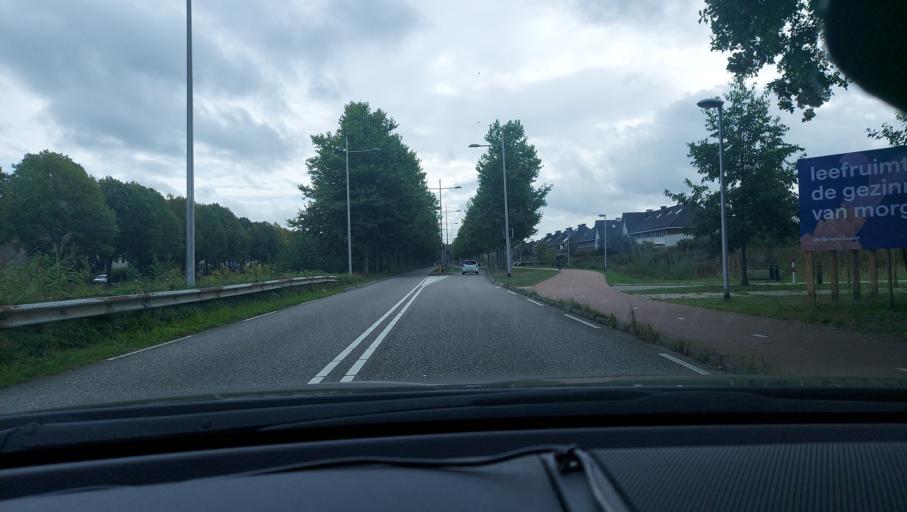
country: NL
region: North Brabant
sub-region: Gemeente Helmond
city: Helmond
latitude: 51.4912
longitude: 5.6517
